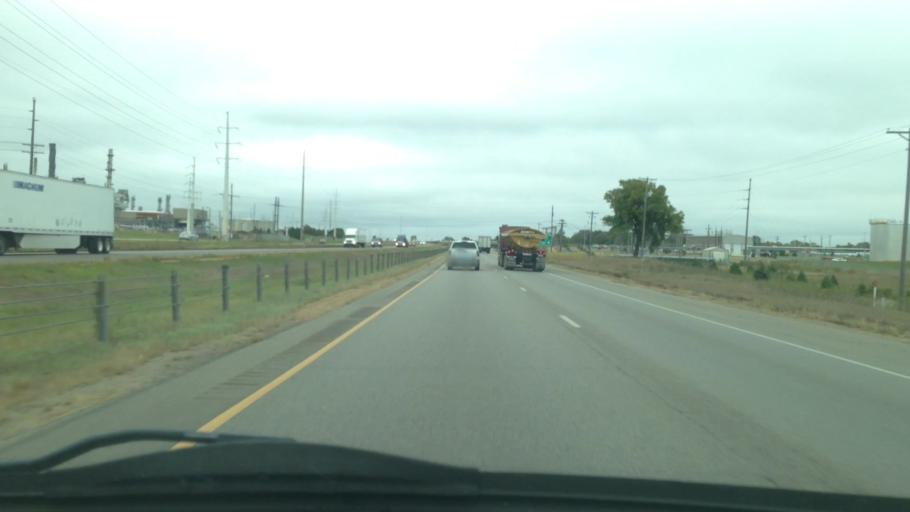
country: US
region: Minnesota
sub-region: Dakota County
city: Inver Grove Heights
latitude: 44.7580
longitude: -93.0339
